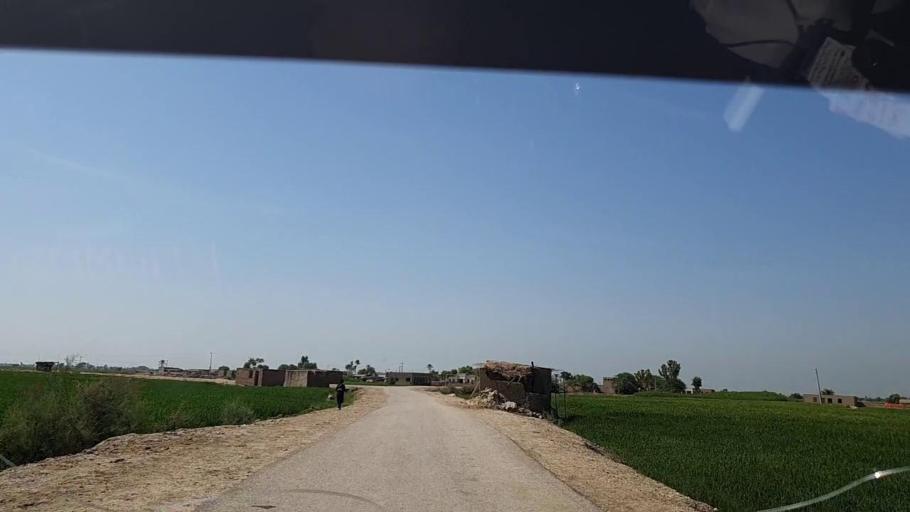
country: PK
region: Sindh
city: Tangwani
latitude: 28.3174
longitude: 69.0933
